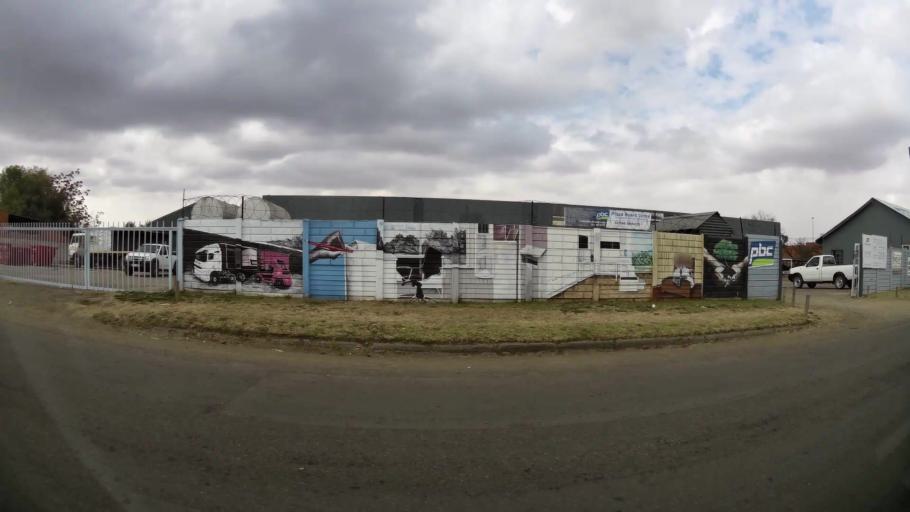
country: ZA
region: Orange Free State
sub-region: Mangaung Metropolitan Municipality
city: Bloemfontein
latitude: -29.1274
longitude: 26.2260
